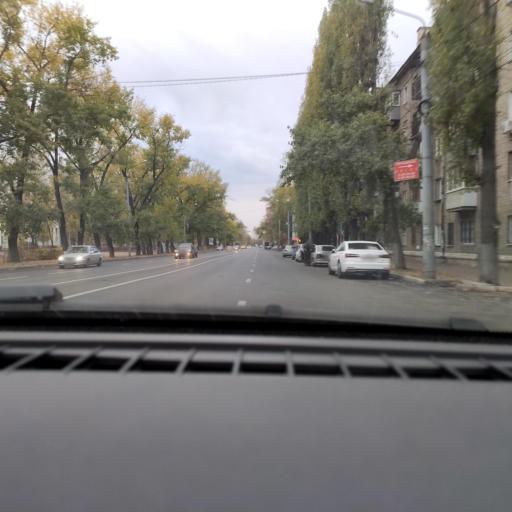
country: RU
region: Voronezj
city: Maslovka
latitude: 51.6123
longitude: 39.2462
